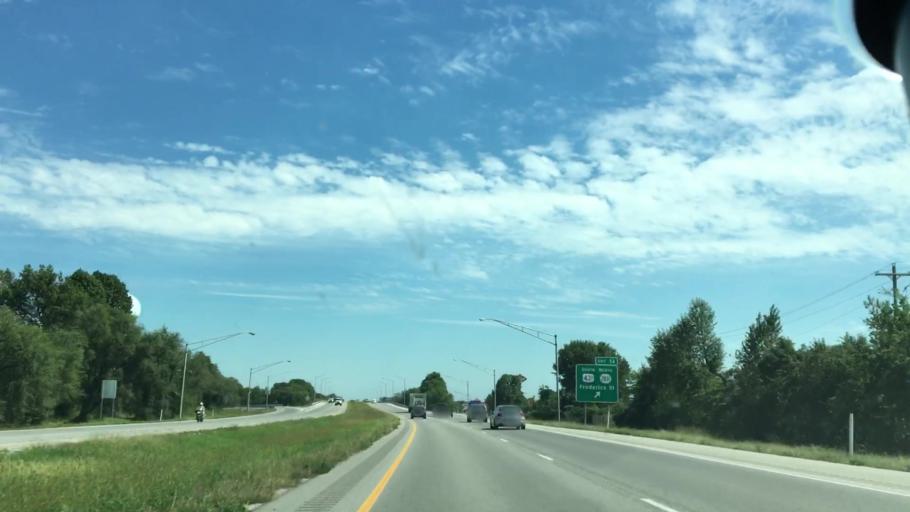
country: US
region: Kentucky
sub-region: Daviess County
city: Owensboro
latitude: 37.7298
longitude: -87.1287
